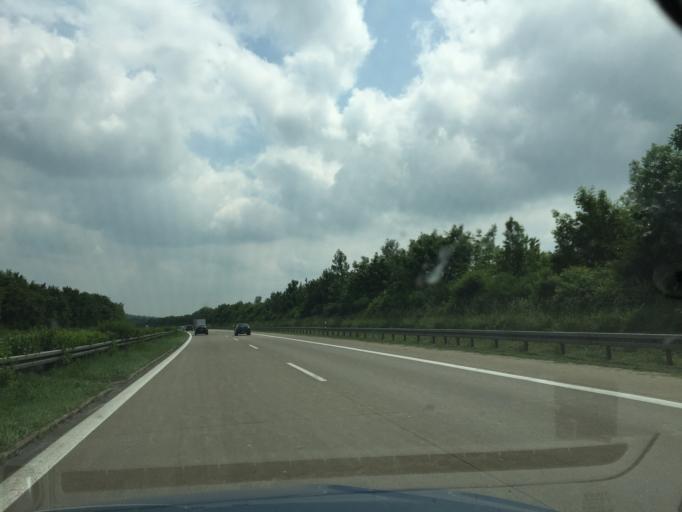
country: DE
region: Baden-Wuerttemberg
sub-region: Regierungsbezirk Stuttgart
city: Westhausen
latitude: 48.8385
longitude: 10.2011
